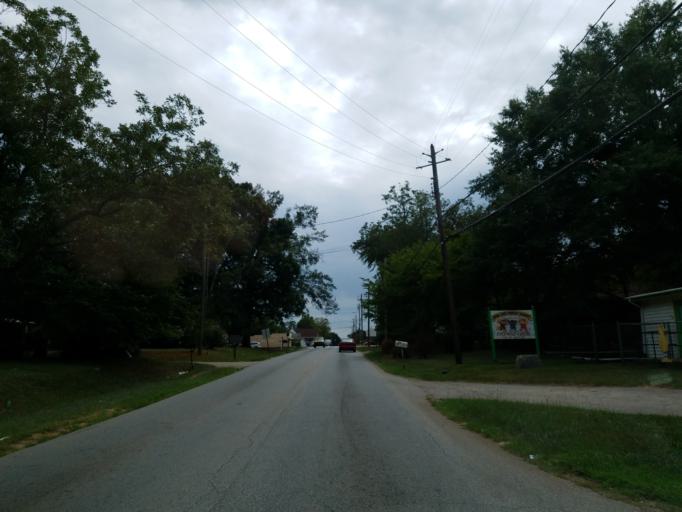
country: US
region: Georgia
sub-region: Spalding County
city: Experiment
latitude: 33.2746
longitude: -84.2847
